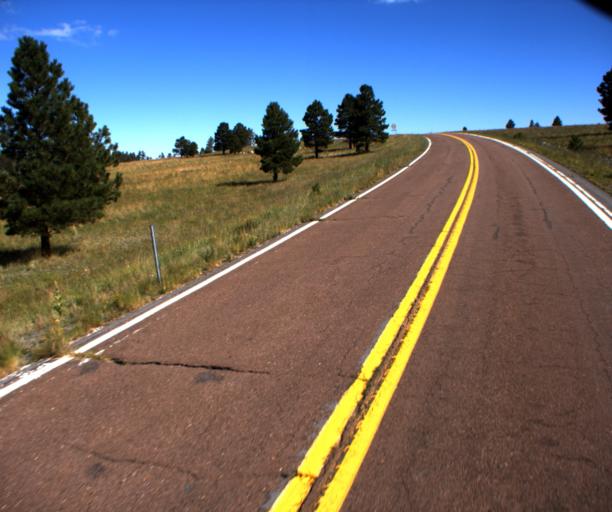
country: US
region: Arizona
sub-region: Apache County
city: Eagar
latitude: 34.0353
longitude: -109.3480
